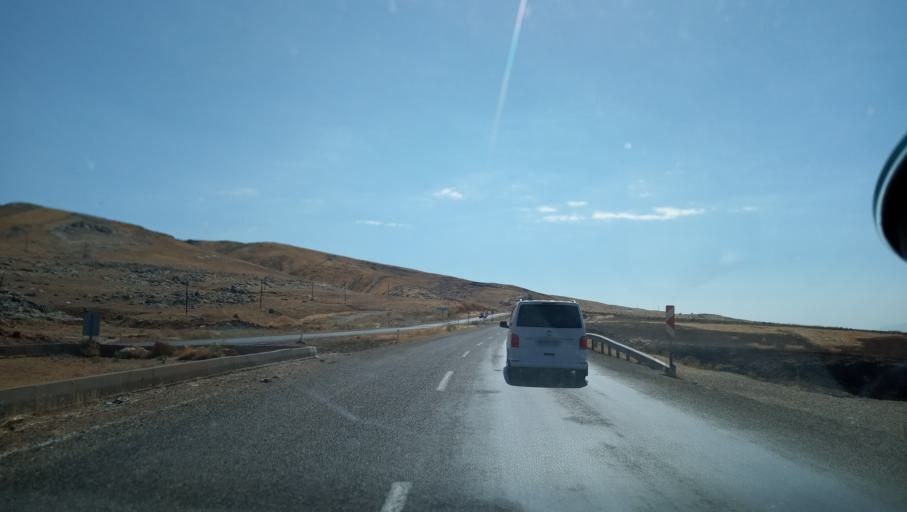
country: TR
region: Diyarbakir
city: Silvan
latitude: 38.1278
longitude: 41.0796
